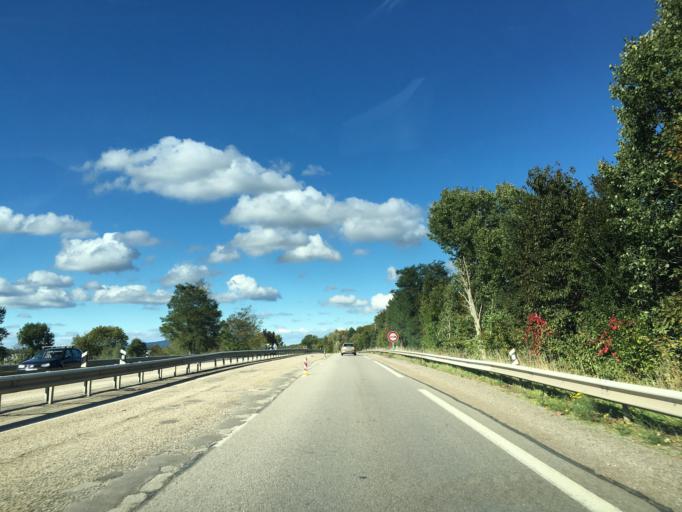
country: FR
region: Lorraine
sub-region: Departement des Vosges
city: Saint-Die-des-Vosges
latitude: 48.2978
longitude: 6.9297
